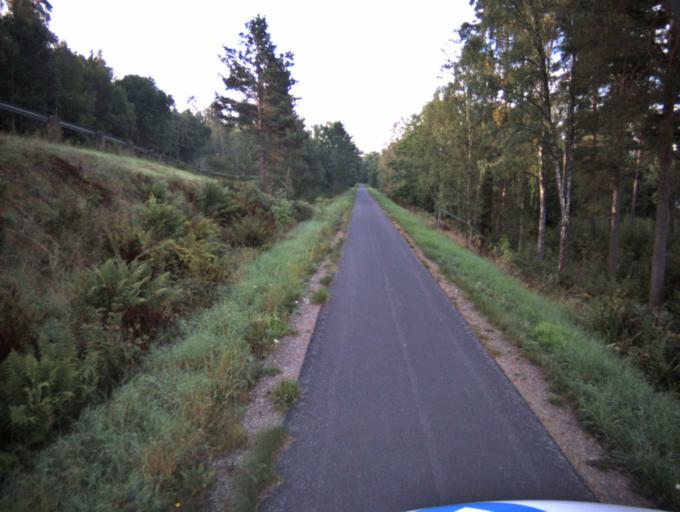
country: SE
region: Vaestra Goetaland
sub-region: Ulricehamns Kommun
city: Ulricehamn
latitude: 57.7491
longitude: 13.3936
